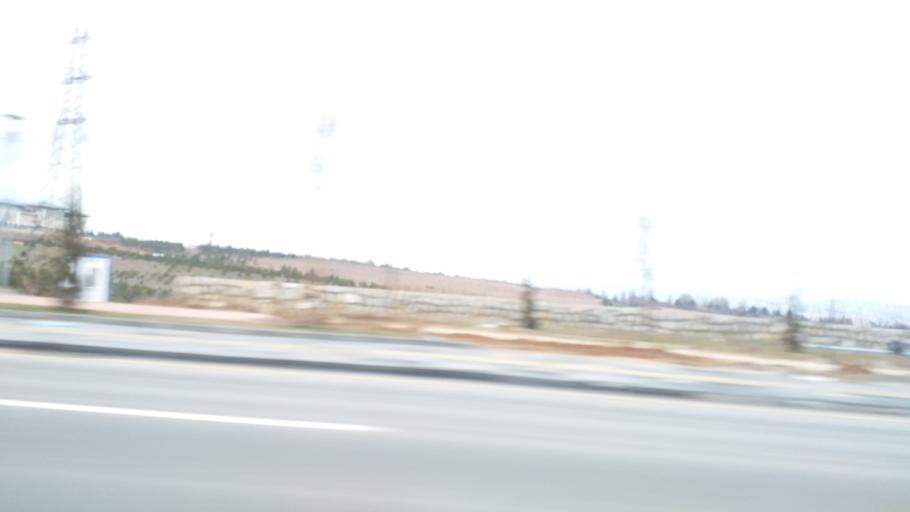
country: TR
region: Ankara
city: Ankara
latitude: 39.9278
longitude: 32.8102
